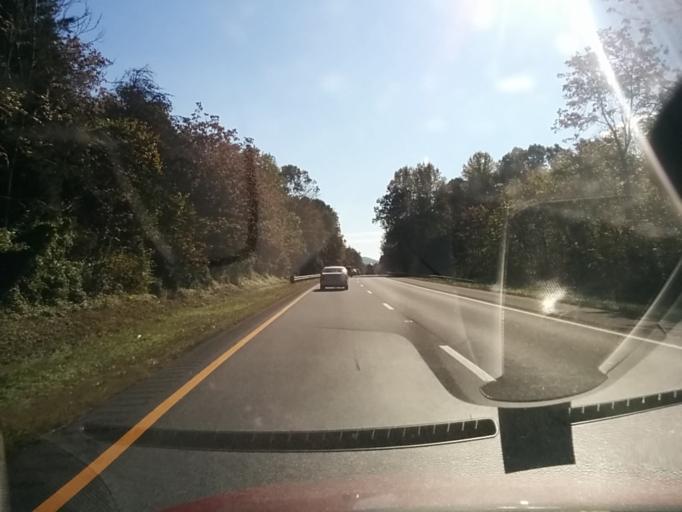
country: US
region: Virginia
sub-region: Albemarle County
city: Crozet
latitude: 38.0458
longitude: -78.7290
